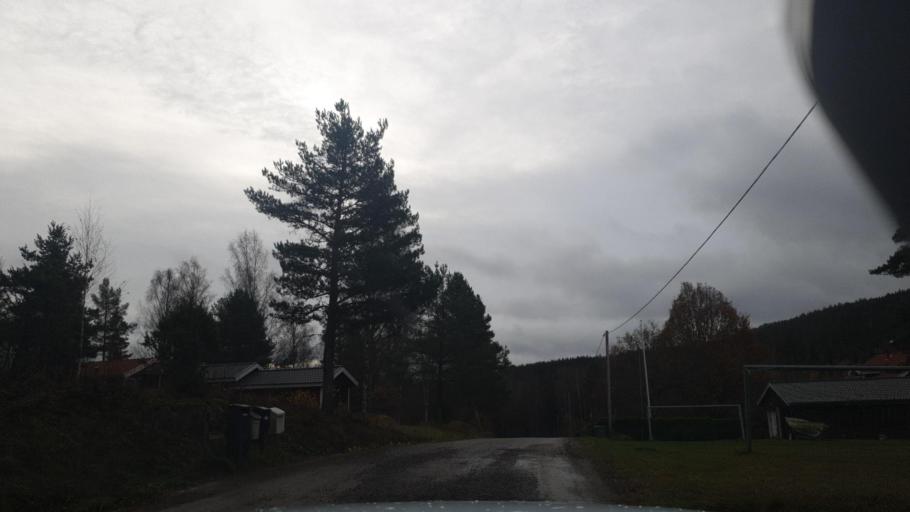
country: NO
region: Ostfold
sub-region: Romskog
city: Romskog
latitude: 59.8111
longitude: 12.0023
